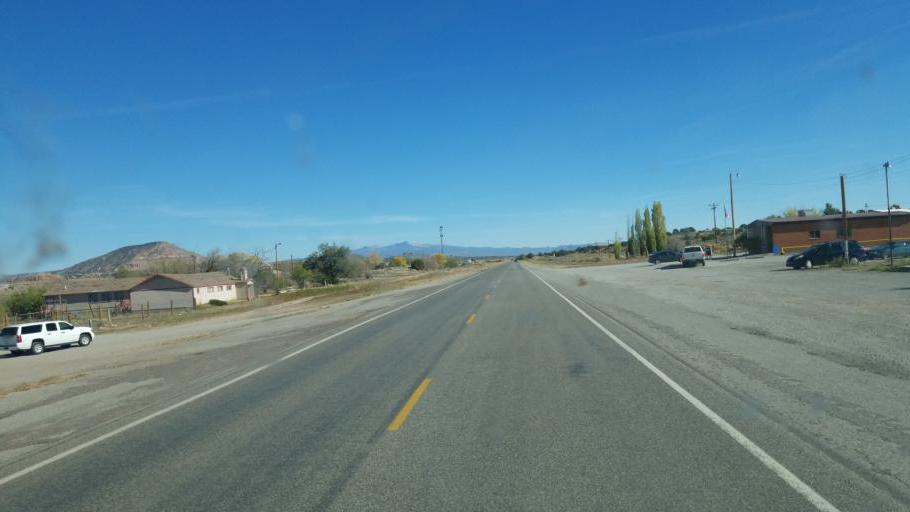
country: US
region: New Mexico
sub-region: McKinley County
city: Thoreau
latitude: 35.3572
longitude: -108.0258
